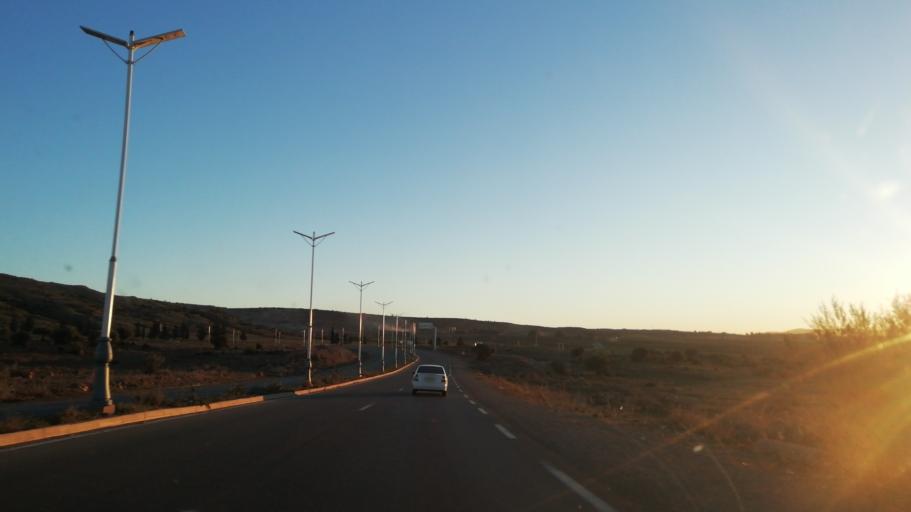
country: DZ
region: Saida
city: Saida
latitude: 34.8558
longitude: 0.1974
